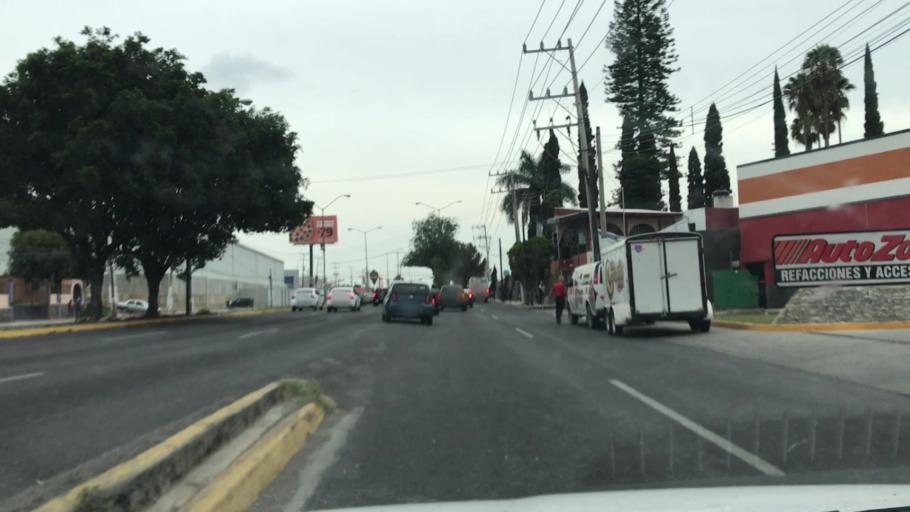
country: MX
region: Jalisco
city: Nuevo Mexico
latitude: 20.7498
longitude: -103.4194
